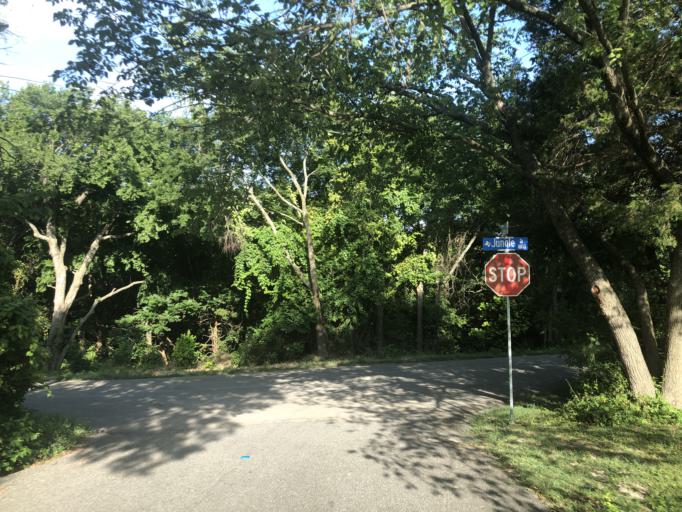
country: US
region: Texas
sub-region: Dallas County
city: Duncanville
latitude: 32.6668
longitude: -96.9216
